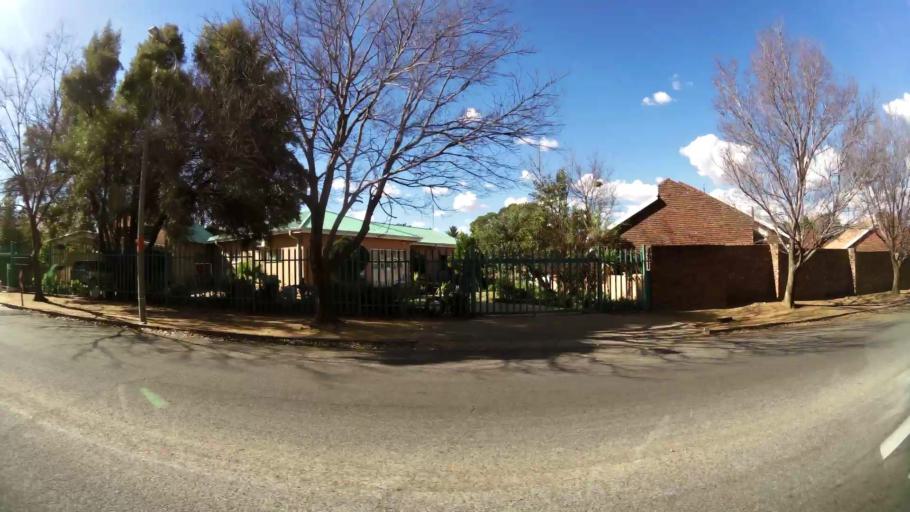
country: ZA
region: North-West
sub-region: Dr Kenneth Kaunda District Municipality
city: Klerksdorp
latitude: -26.8614
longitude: 26.6478
